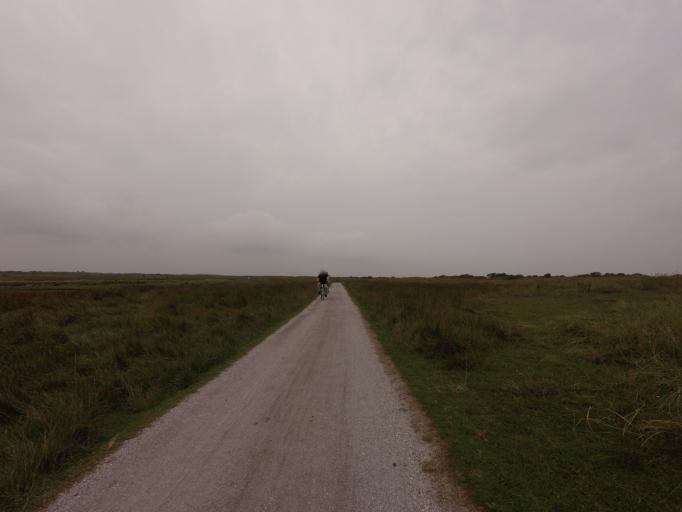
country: NL
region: Friesland
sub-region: Gemeente Schiermonnikoog
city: Schiermonnikoog
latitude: 53.4866
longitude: 6.2134
